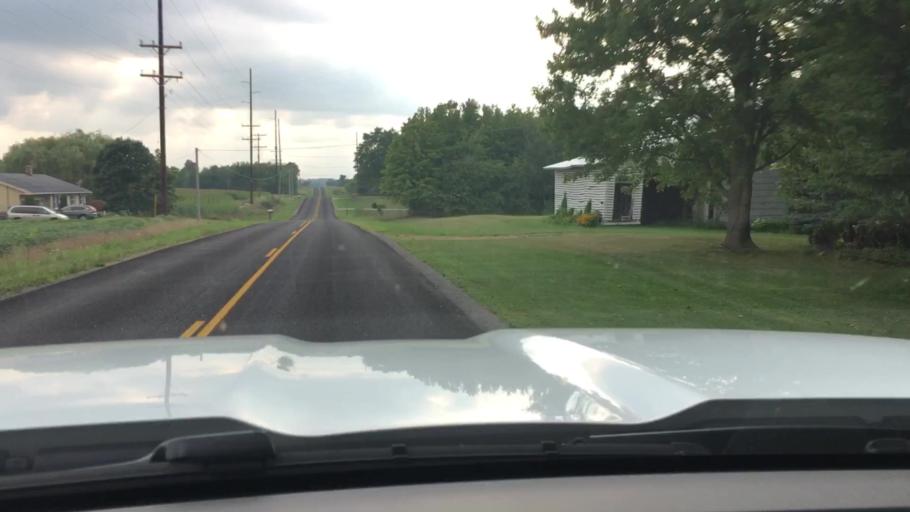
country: US
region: Michigan
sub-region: Ottawa County
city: Hudsonville
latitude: 42.8331
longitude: -85.8678
